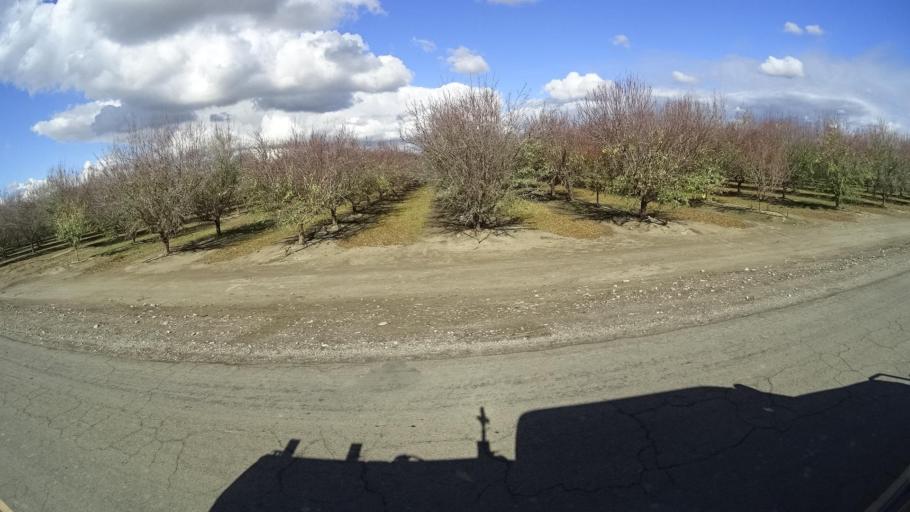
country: US
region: California
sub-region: Kern County
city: Greenfield
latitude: 35.2235
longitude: -119.1042
